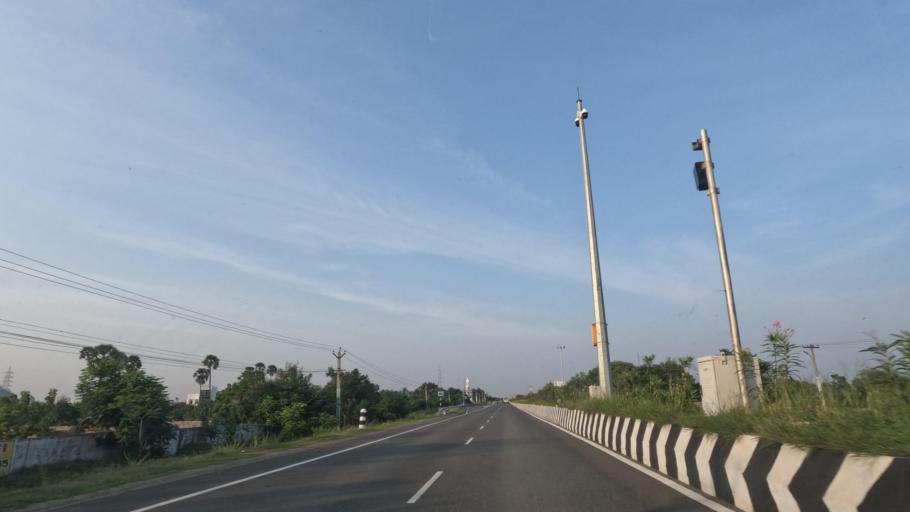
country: IN
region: Tamil Nadu
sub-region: Kancheepuram
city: Mamallapuram
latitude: 12.6968
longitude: 80.2204
